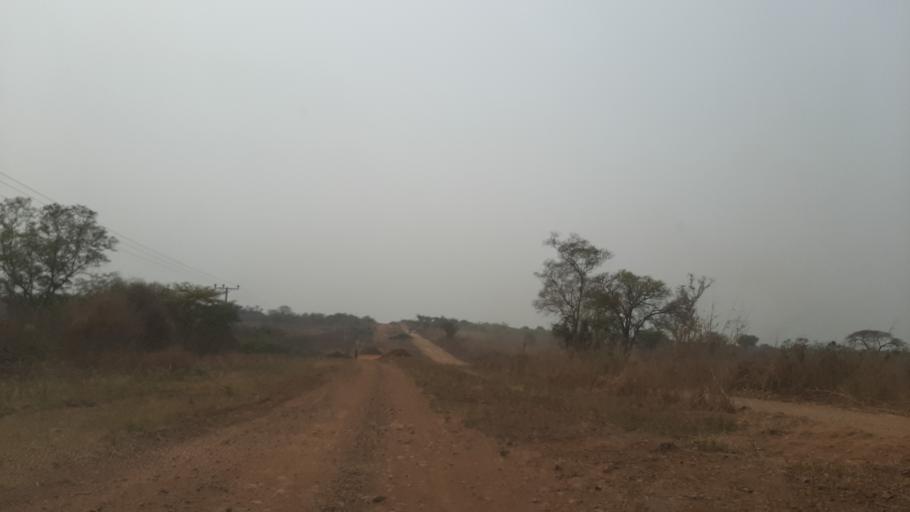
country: ET
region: Gambela
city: Gambela
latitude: 8.2224
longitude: 34.5374
